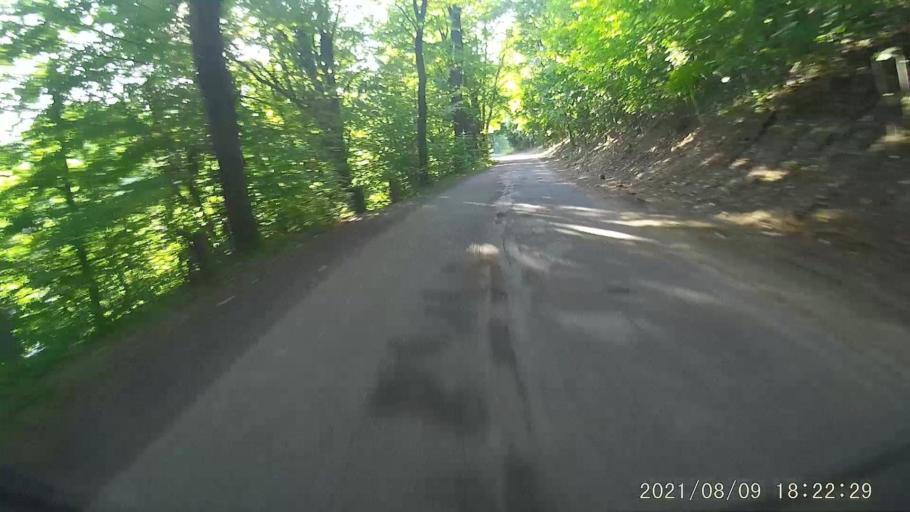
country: PL
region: Lower Silesian Voivodeship
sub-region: Powiat zabkowicki
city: Bardo
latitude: 50.5044
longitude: 16.7111
